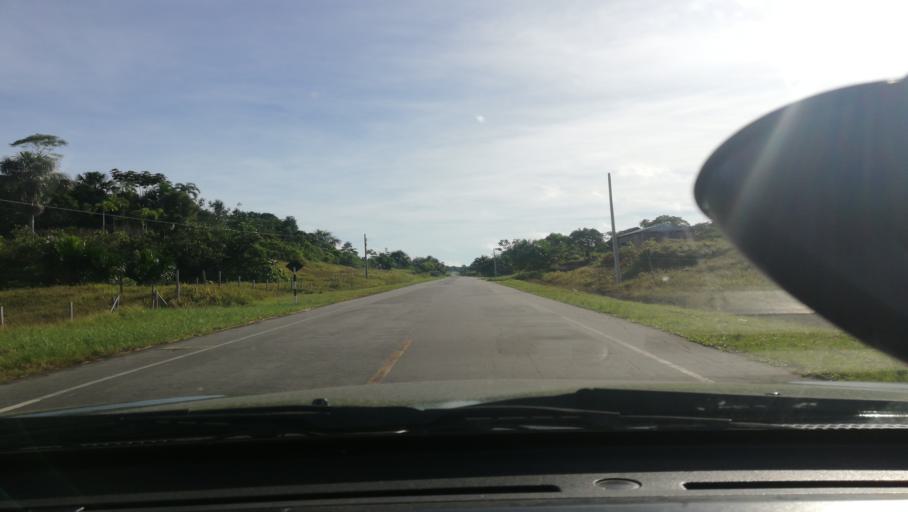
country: PE
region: Loreto
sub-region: Provincia de Loreto
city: Nauta
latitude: -4.3429
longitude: -73.5397
